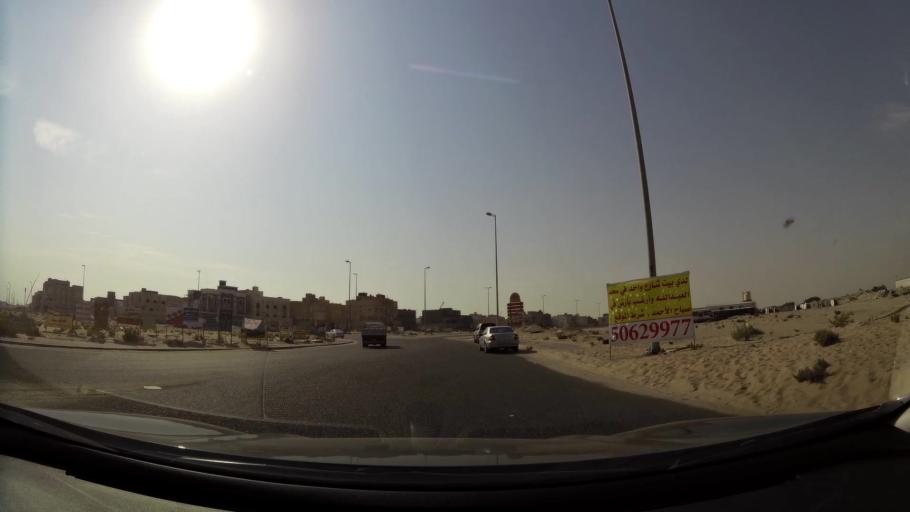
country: KW
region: Al Ahmadi
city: Al Wafrah
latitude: 28.7909
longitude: 48.0368
